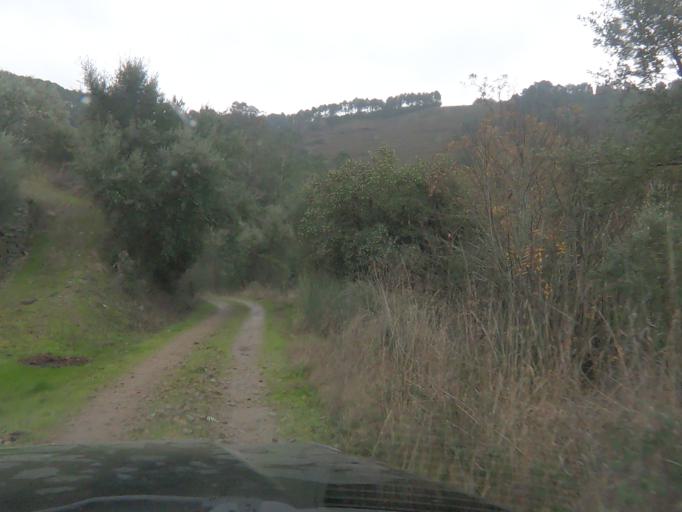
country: PT
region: Vila Real
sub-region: Vila Real
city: Vila Real
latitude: 41.2697
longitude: -7.7381
